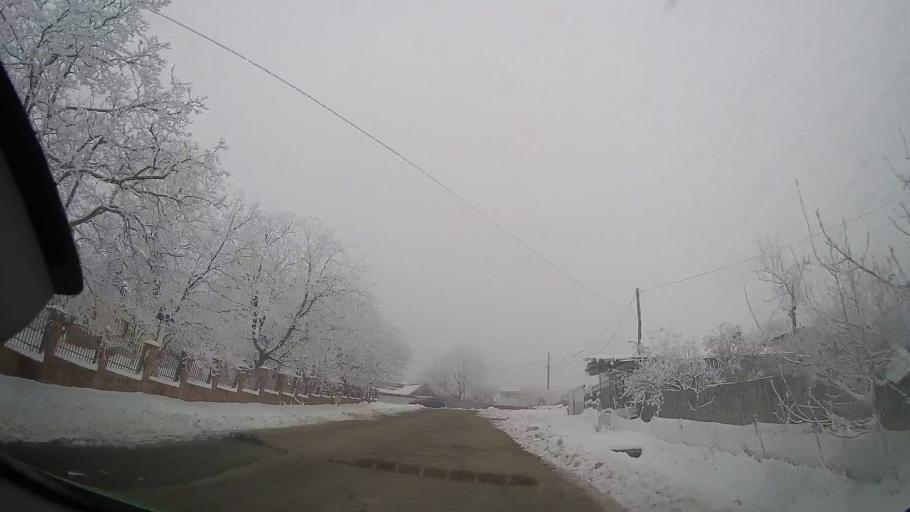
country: RO
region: Neamt
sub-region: Comuna Valea Ursului
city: Valea Ursului
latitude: 46.7966
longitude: 27.0815
